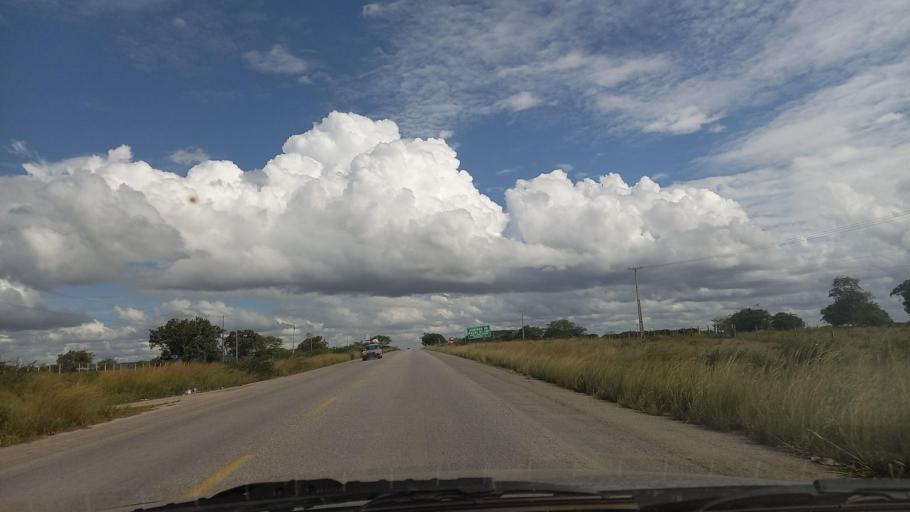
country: BR
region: Pernambuco
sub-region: Cachoeirinha
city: Cachoeirinha
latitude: -8.4636
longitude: -36.2166
